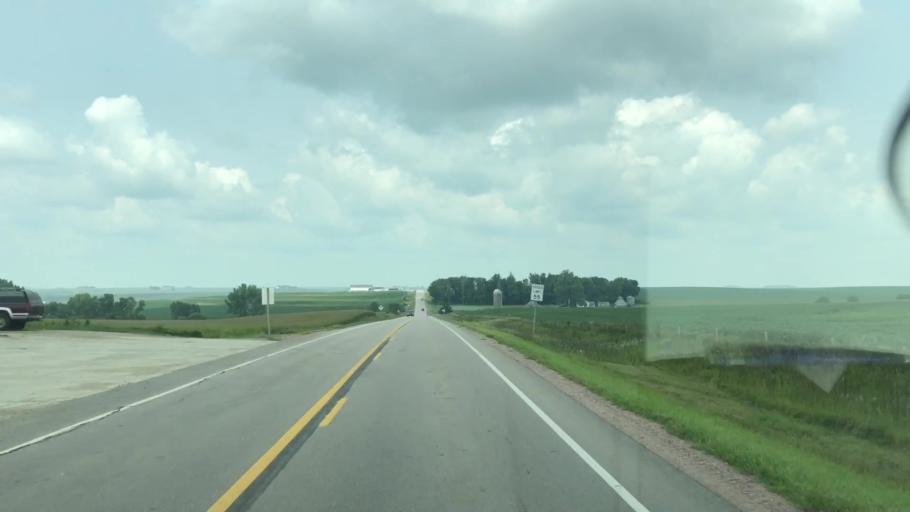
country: US
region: Iowa
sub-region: Plymouth County
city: Kingsley
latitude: 42.5932
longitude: -95.9573
